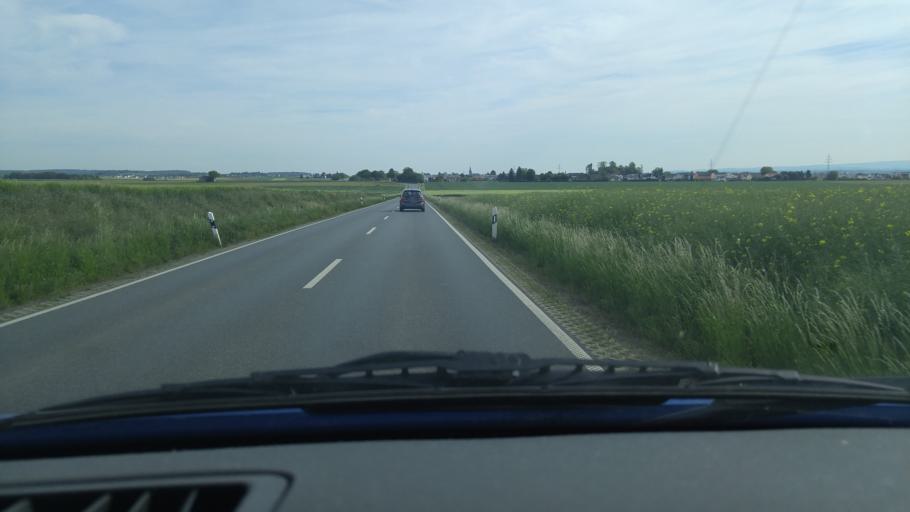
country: DE
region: Hesse
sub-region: Regierungsbezirk Darmstadt
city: Wolfersheim
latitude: 50.3696
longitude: 8.8003
